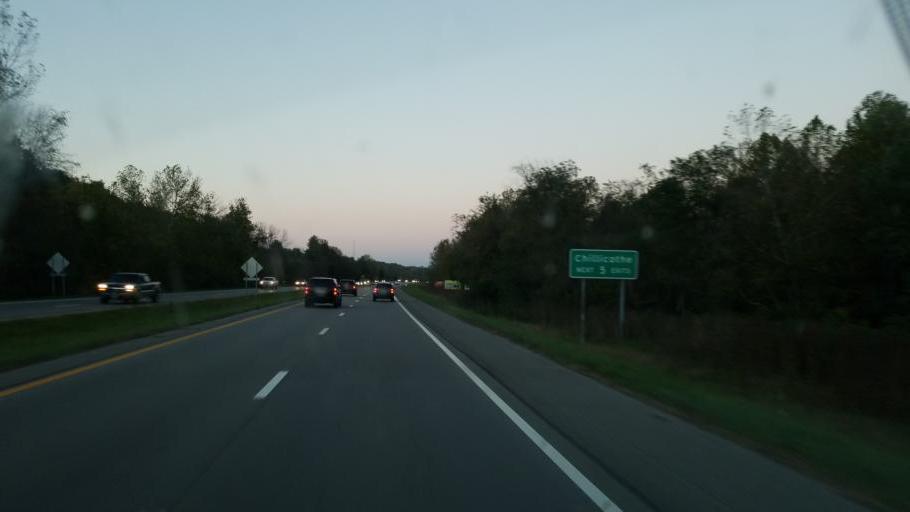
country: US
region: Ohio
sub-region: Ross County
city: Chillicothe
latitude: 39.2708
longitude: -82.9645
